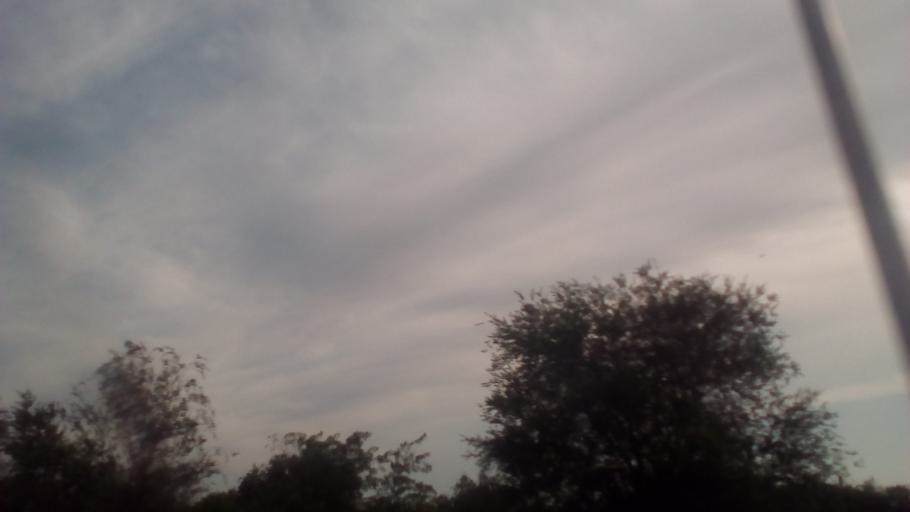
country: KZ
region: Ongtustik Qazaqstan
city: Temirlanovka
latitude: 42.7967
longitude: 69.1997
